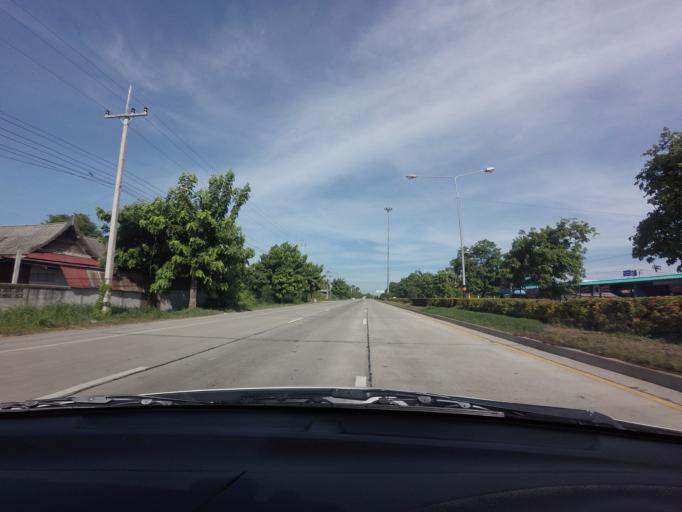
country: TH
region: Suphan Buri
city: Suphan Buri
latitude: 14.4550
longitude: 100.0784
